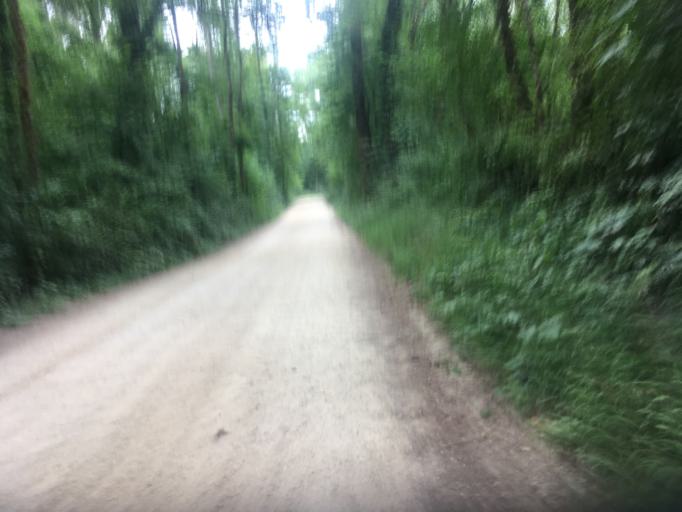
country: CH
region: Bern
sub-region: Jura bernois
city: La Neuveville
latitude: 47.0614
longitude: 7.1325
